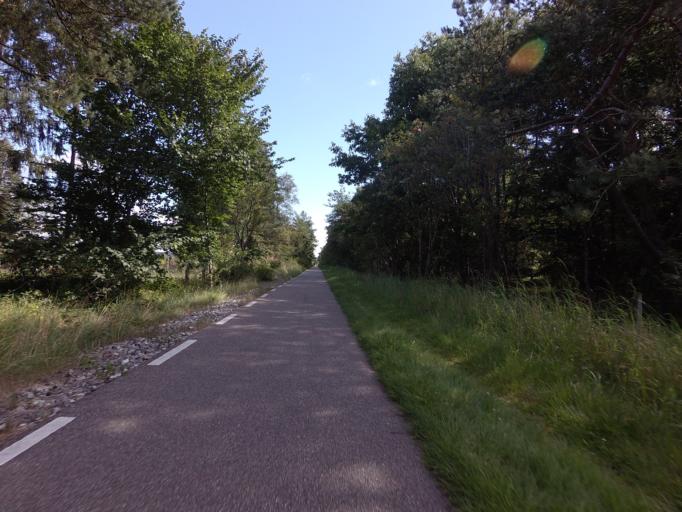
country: DK
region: Central Jutland
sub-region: Silkeborg Kommune
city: Svejbaek
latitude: 56.1736
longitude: 9.6222
